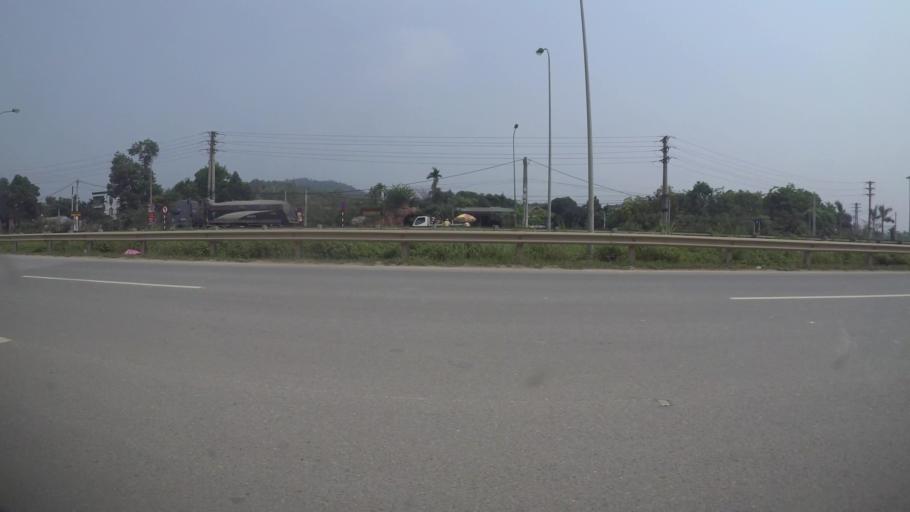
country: VN
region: Ha Noi
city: Lien Quan
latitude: 20.9905
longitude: 105.5201
